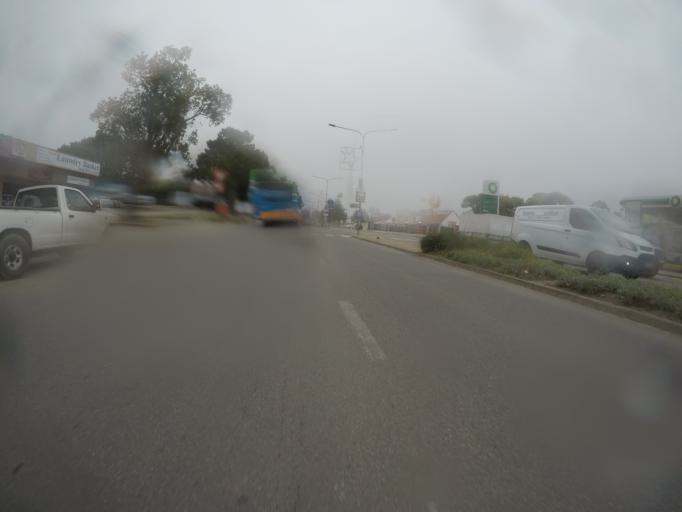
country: ZA
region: Western Cape
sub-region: Eden District Municipality
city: George
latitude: -33.9709
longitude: 22.4472
